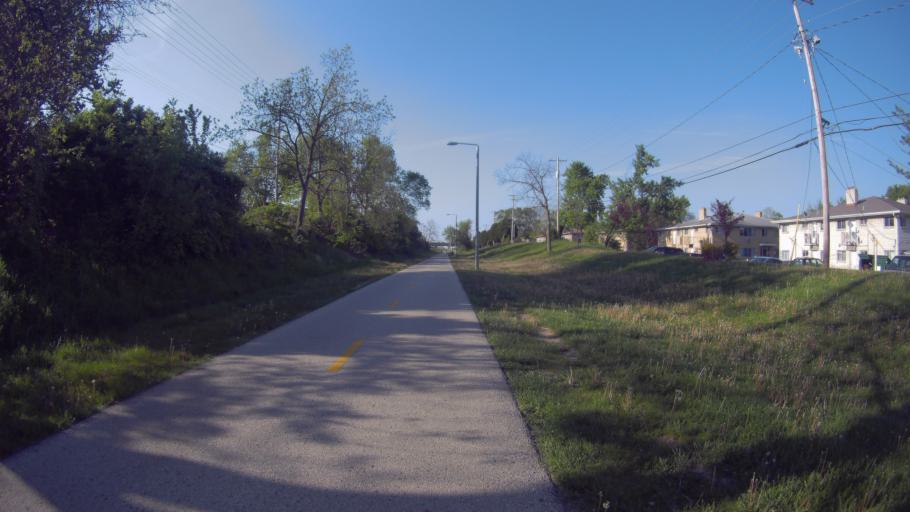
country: US
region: Wisconsin
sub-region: Dane County
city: Shorewood Hills
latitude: 43.0278
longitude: -89.4606
